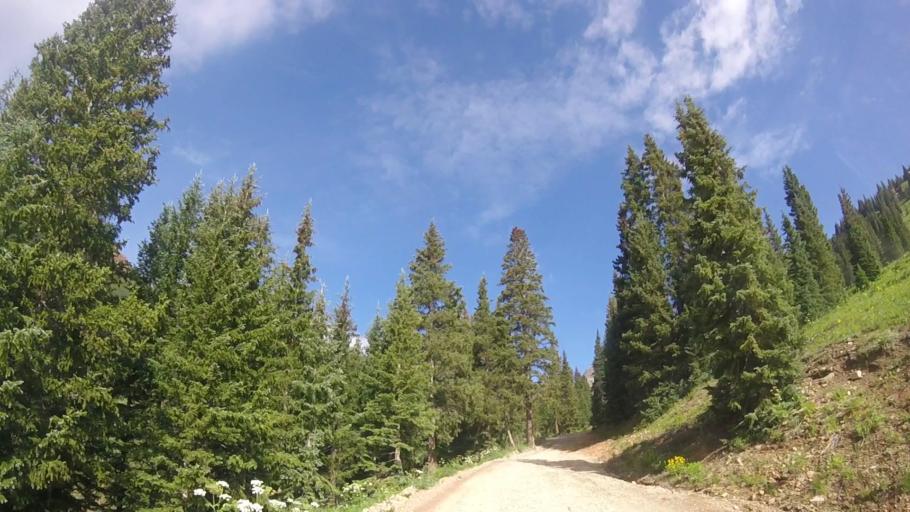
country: US
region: Colorado
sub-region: San Miguel County
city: Telluride
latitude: 37.8463
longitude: -107.7681
